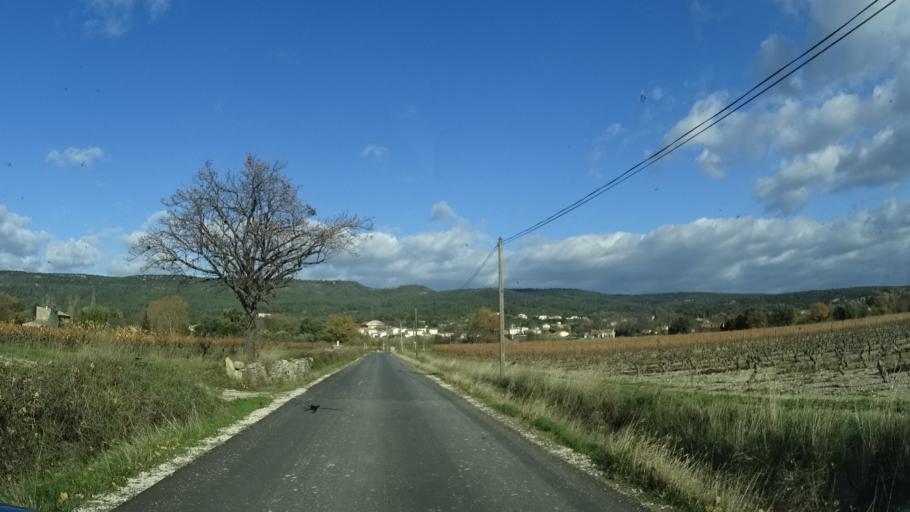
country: FR
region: Languedoc-Roussillon
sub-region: Departement de l'Herault
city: Claret
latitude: 43.8556
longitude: 3.8967
